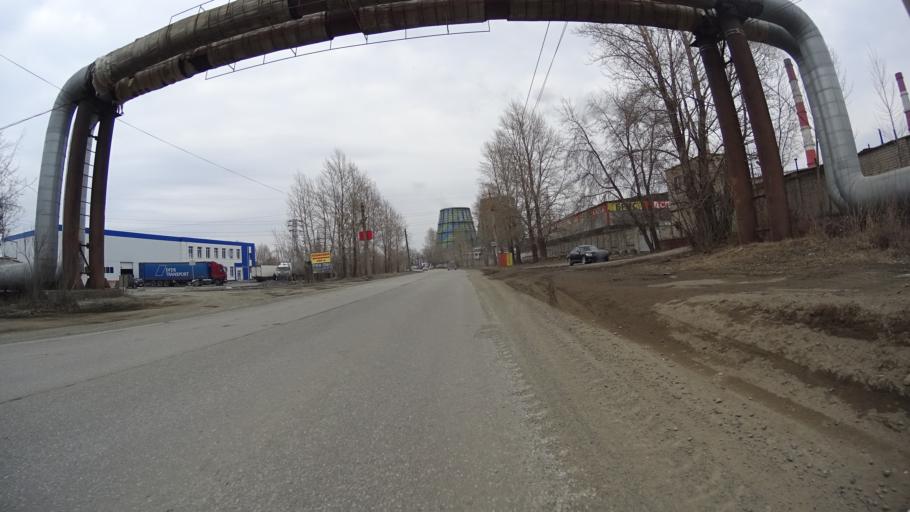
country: RU
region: Chelyabinsk
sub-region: Gorod Chelyabinsk
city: Chelyabinsk
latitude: 55.1567
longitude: 61.4944
